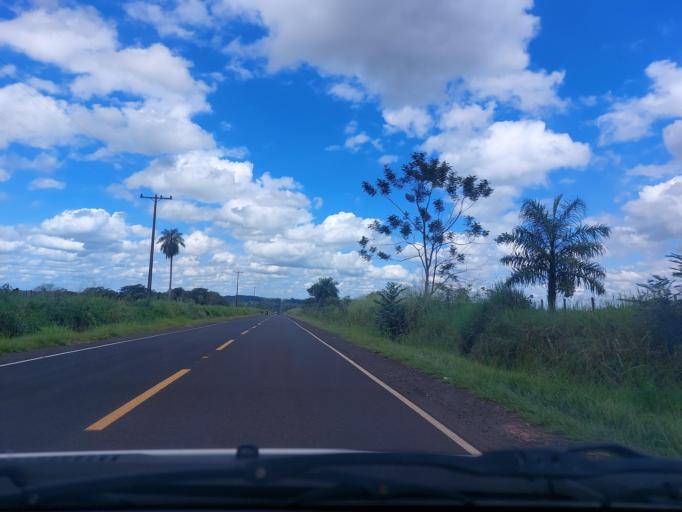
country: PY
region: San Pedro
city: Guayaybi
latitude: -24.5352
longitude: -56.5198
